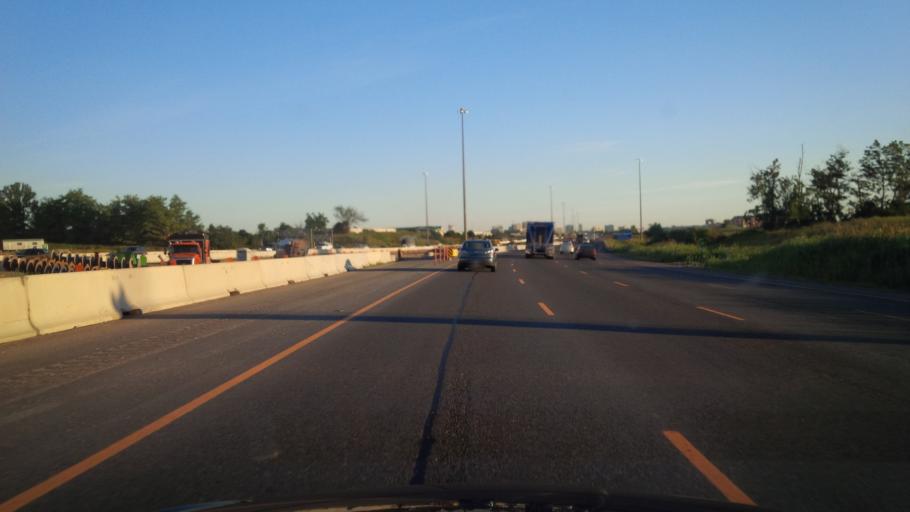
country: CA
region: Ontario
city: Brampton
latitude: 43.6716
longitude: -79.7027
